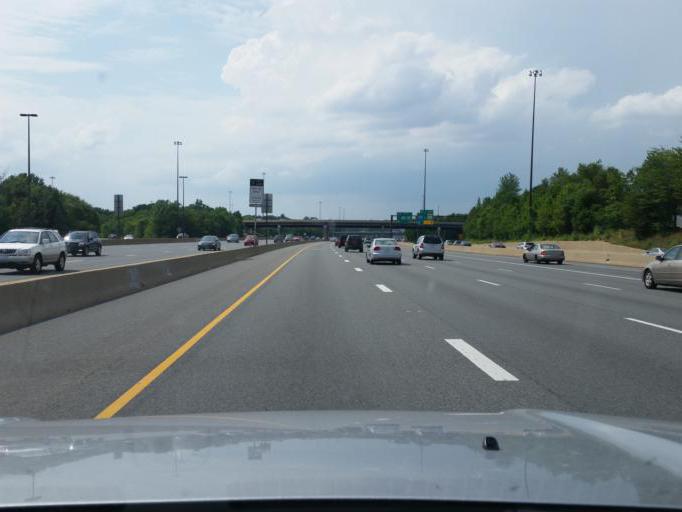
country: US
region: Maryland
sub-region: Montgomery County
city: Gaithersburg
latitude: 39.1167
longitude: -77.1940
